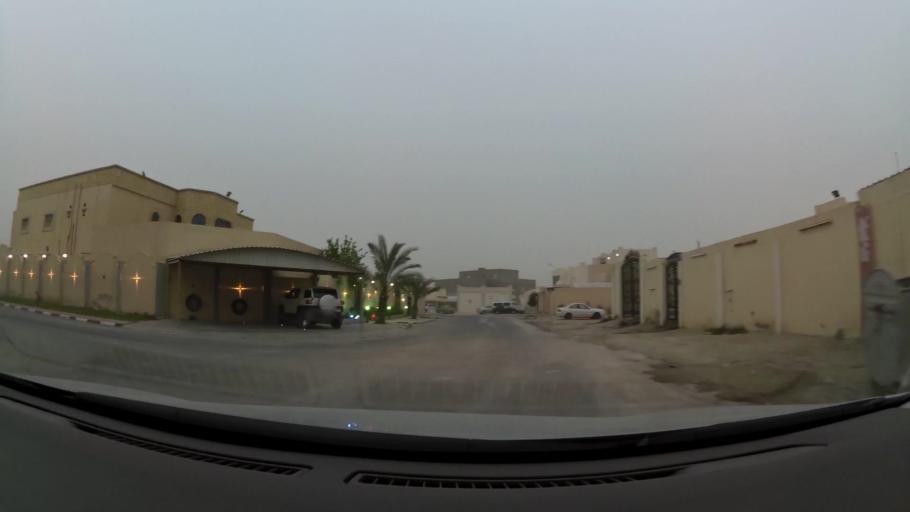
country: QA
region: Baladiyat ad Dawhah
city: Doha
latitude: 25.2299
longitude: 51.4964
